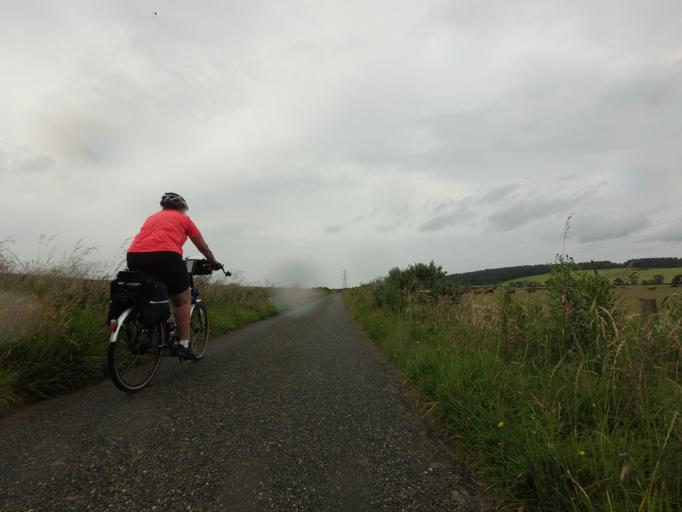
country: GB
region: Scotland
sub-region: Moray
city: Cullen
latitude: 57.6735
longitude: -2.7866
